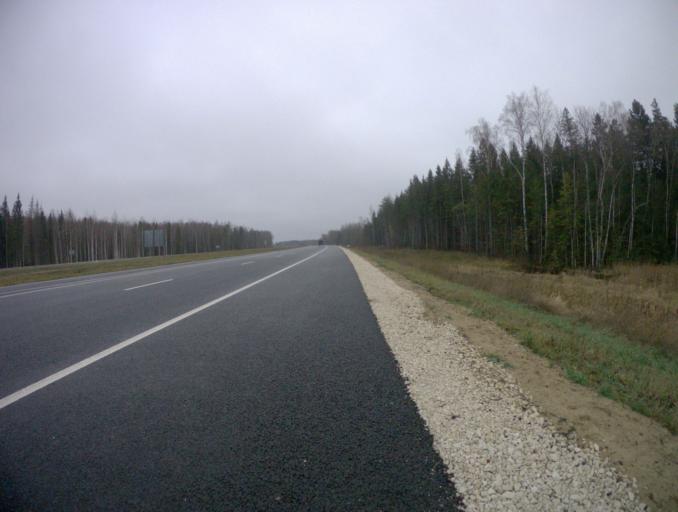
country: RU
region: Vladimir
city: Kommunar
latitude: 56.0458
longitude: 40.5190
